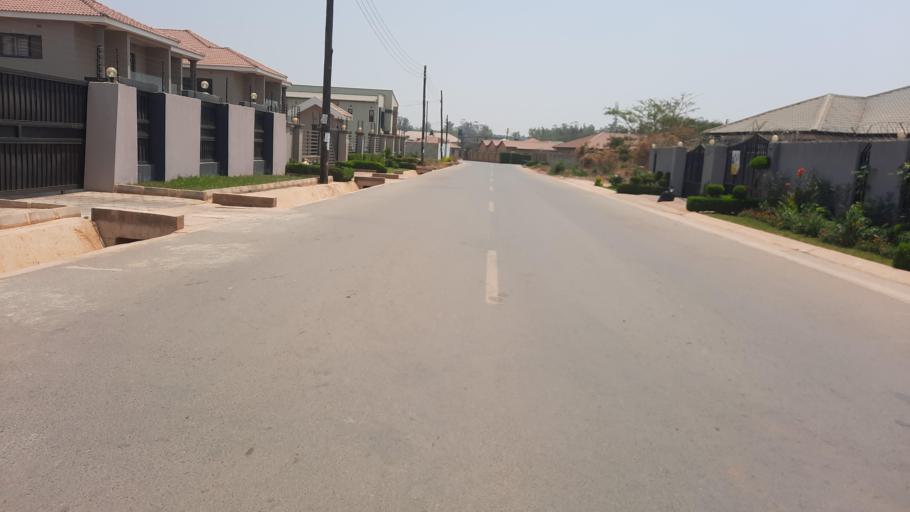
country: ZM
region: Lusaka
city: Lusaka
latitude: -15.3932
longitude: 28.3849
